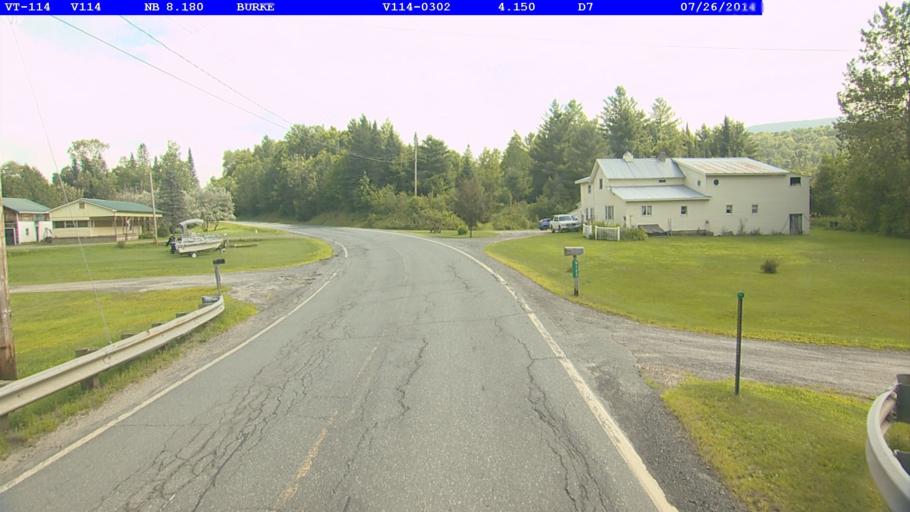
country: US
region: Vermont
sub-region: Caledonia County
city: Lyndonville
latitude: 44.6281
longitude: -71.9020
